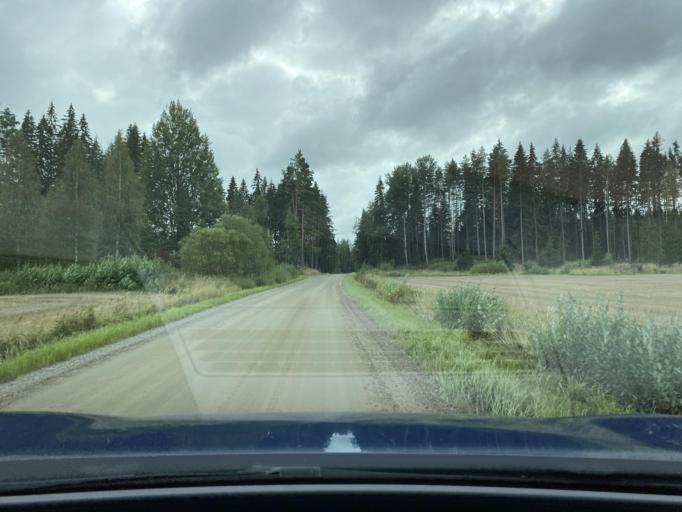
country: FI
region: Pirkanmaa
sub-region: Lounais-Pirkanmaa
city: Punkalaidun
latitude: 61.1790
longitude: 23.1822
